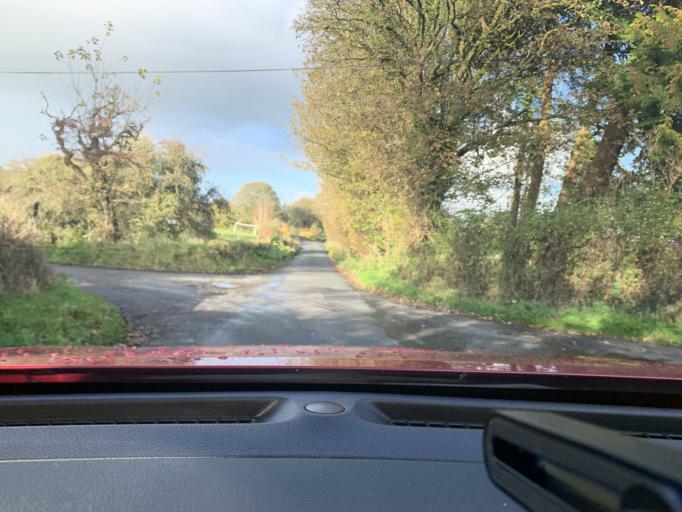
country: IE
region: Connaught
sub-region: Sligo
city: Ballymote
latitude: 54.0991
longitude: -8.4357
